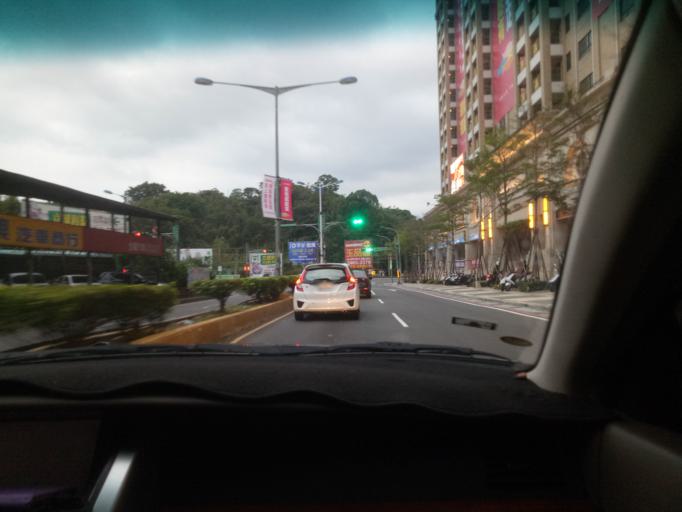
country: TW
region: Taiwan
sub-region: Keelung
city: Keelung
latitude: 25.1284
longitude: 121.7797
